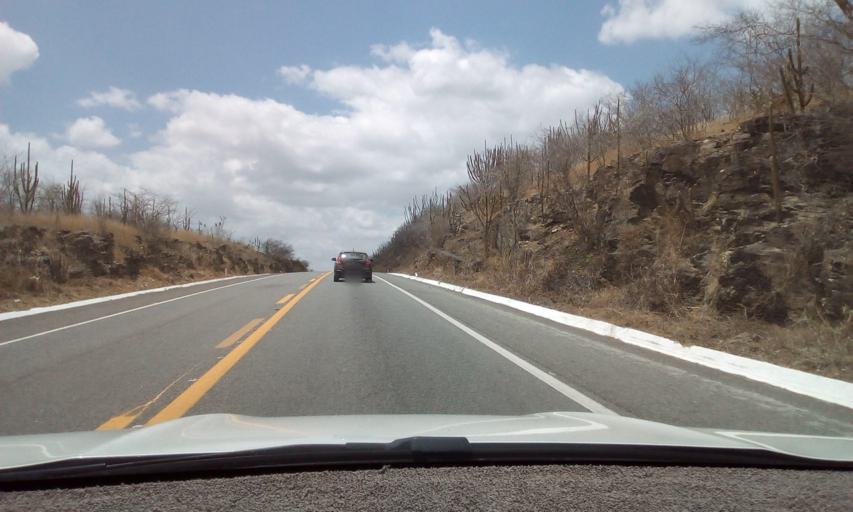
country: BR
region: Paraiba
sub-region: Boqueirao
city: Boqueirao
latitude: -7.6374
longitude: -36.0783
